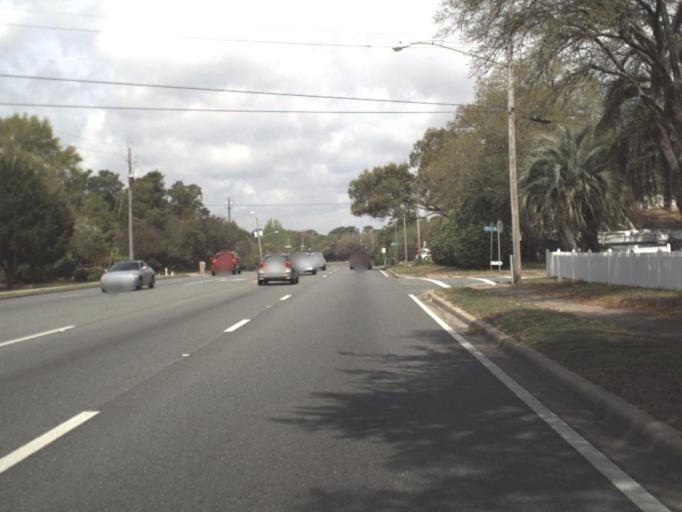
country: US
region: Florida
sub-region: Okaloosa County
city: Ocean City
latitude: 30.4250
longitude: -86.6177
